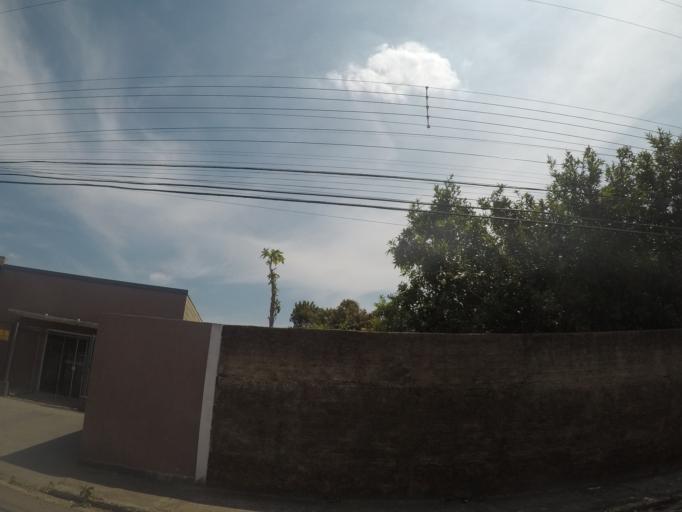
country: BR
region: Sao Paulo
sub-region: Itupeva
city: Itupeva
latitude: -23.2460
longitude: -47.0619
